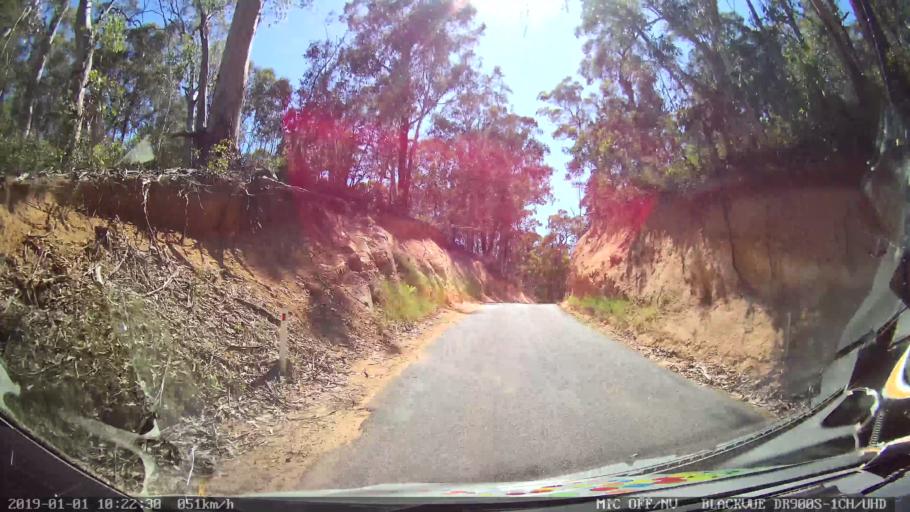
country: AU
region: New South Wales
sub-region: Snowy River
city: Jindabyne
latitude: -36.0776
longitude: 148.2042
